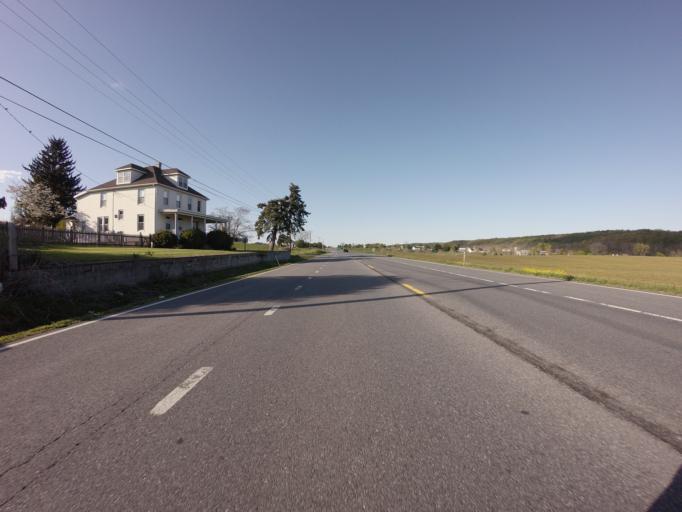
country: US
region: Maryland
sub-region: Frederick County
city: Woodsboro
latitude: 39.5133
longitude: -77.3197
